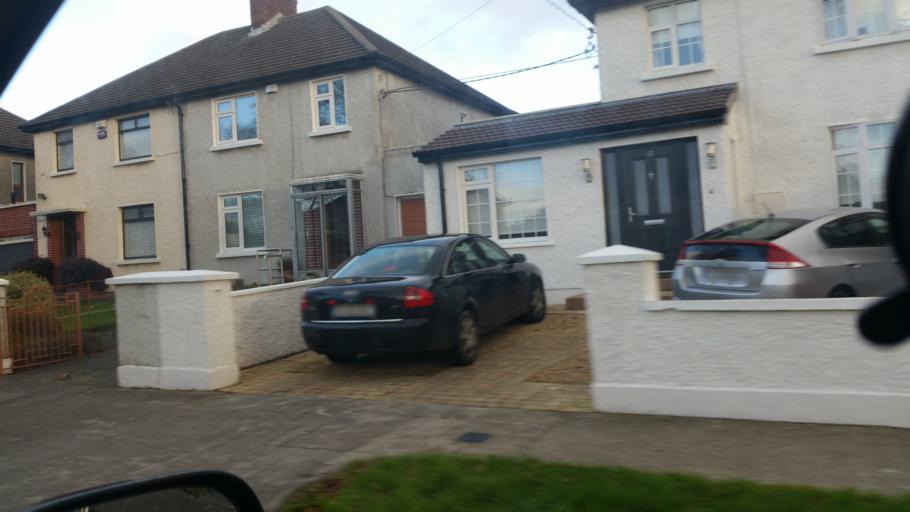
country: IE
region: Leinster
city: Beaumont
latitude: 53.3837
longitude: -6.2294
